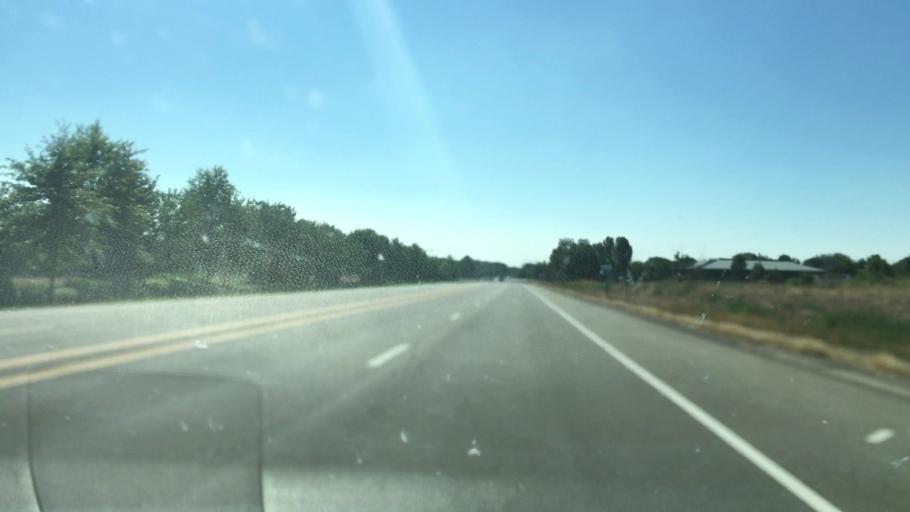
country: US
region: Idaho
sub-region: Ada County
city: Eagle
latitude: 43.6902
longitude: -116.3464
